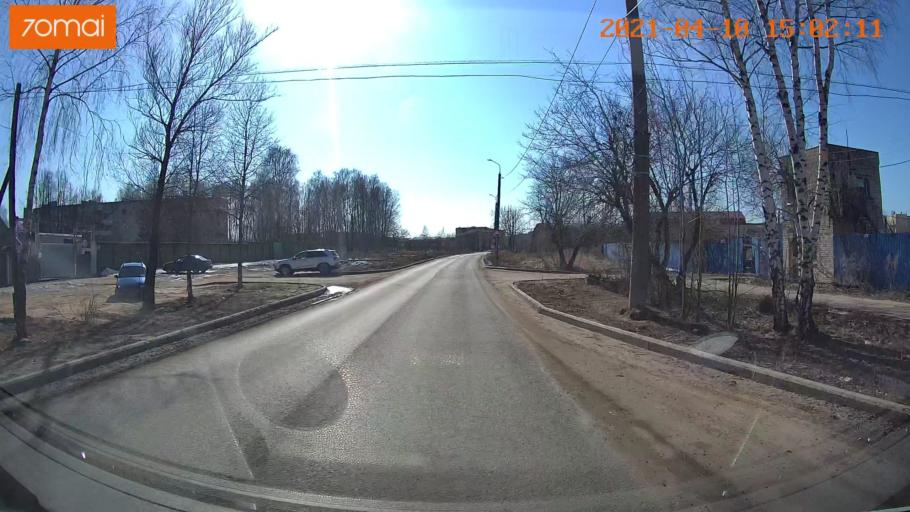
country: RU
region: Ivanovo
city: Bogorodskoye
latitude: 56.9967
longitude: 41.0477
